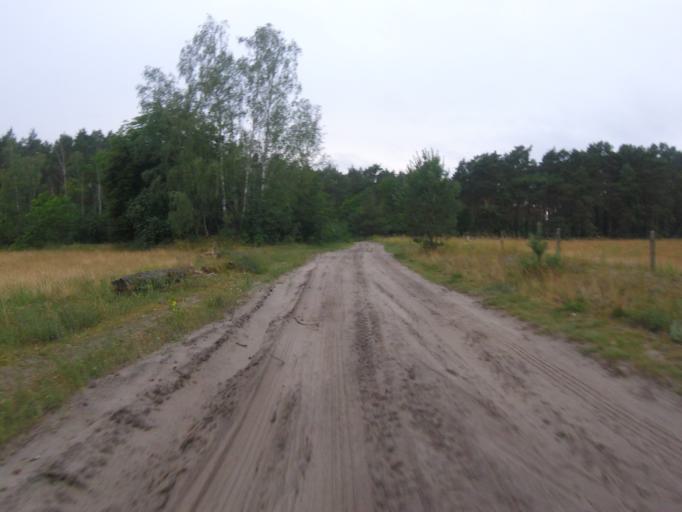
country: DE
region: Brandenburg
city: Schwerin
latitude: 52.1938
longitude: 13.6287
